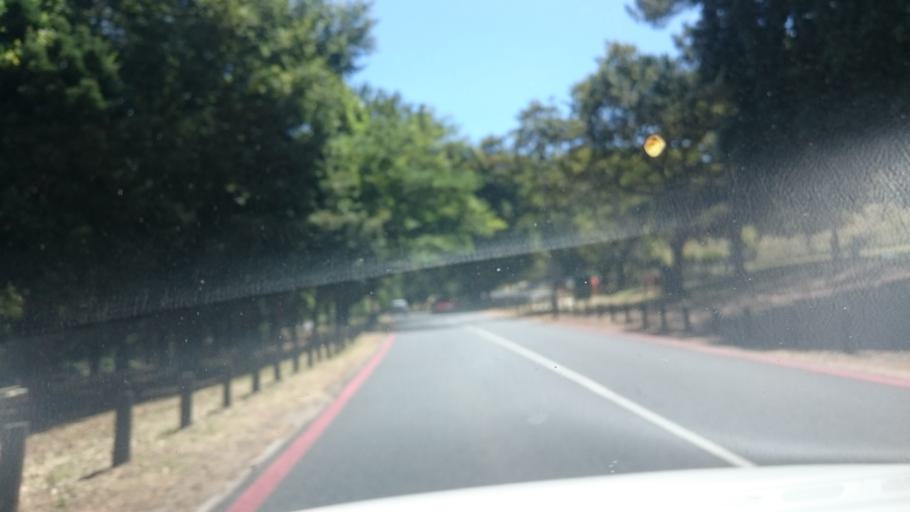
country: ZA
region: Western Cape
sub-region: City of Cape Town
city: Newlands
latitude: -33.9991
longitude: 18.4532
